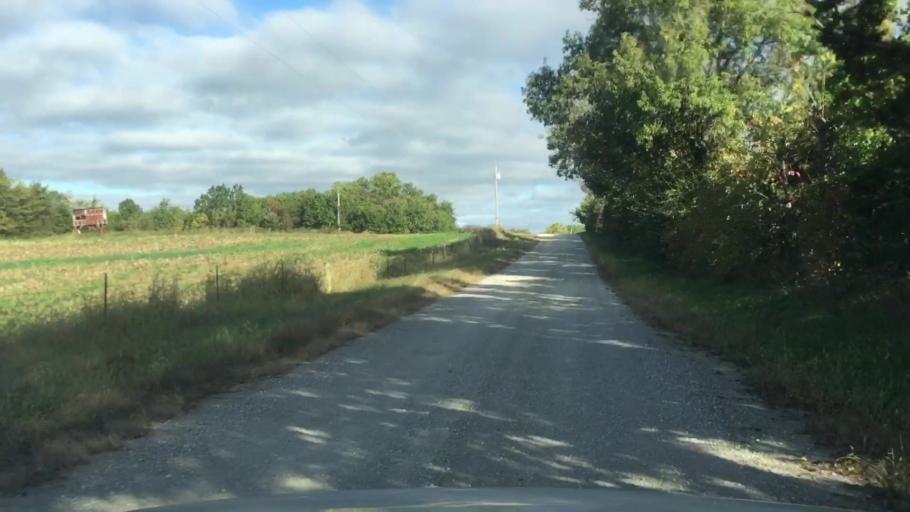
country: US
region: Missouri
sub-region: Howard County
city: New Franklin
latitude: 39.0885
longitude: -92.7830
